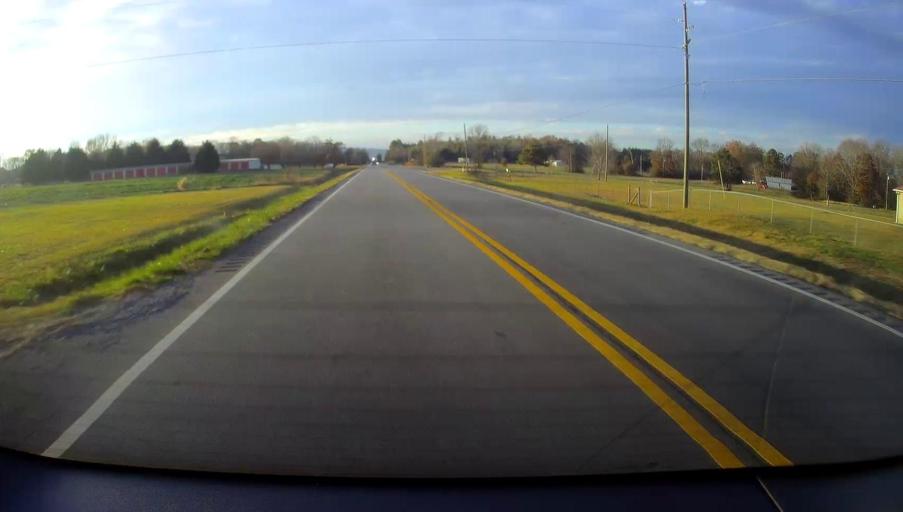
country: US
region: Alabama
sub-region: Saint Clair County
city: Steele
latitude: 34.0620
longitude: -86.2388
